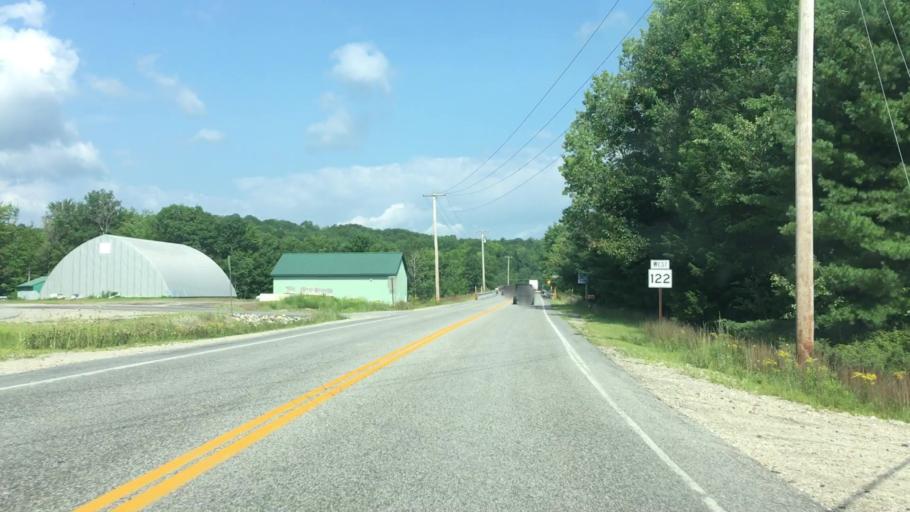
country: US
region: Maine
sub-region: Cumberland County
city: New Gloucester
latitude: 44.0262
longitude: -70.2864
